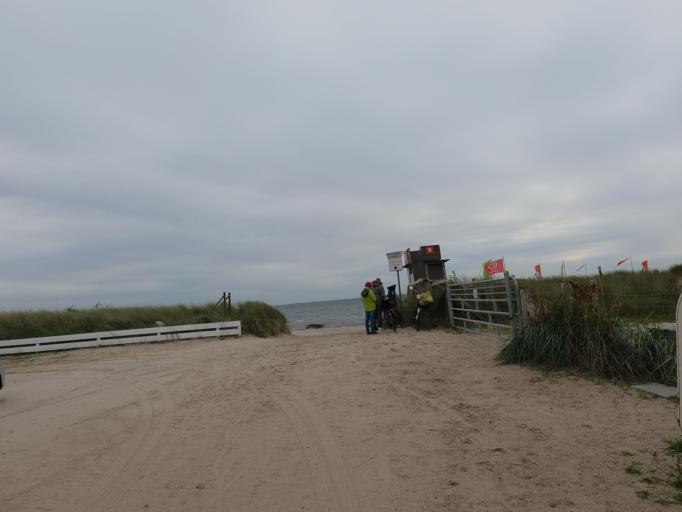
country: DE
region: Schleswig-Holstein
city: Gromitz
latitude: 54.1546
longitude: 10.9898
